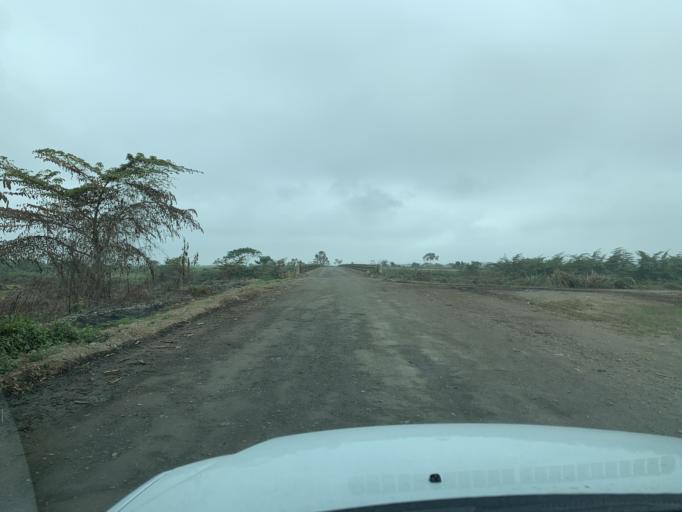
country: EC
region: Guayas
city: Coronel Marcelino Mariduena
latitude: -2.3593
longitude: -79.5823
